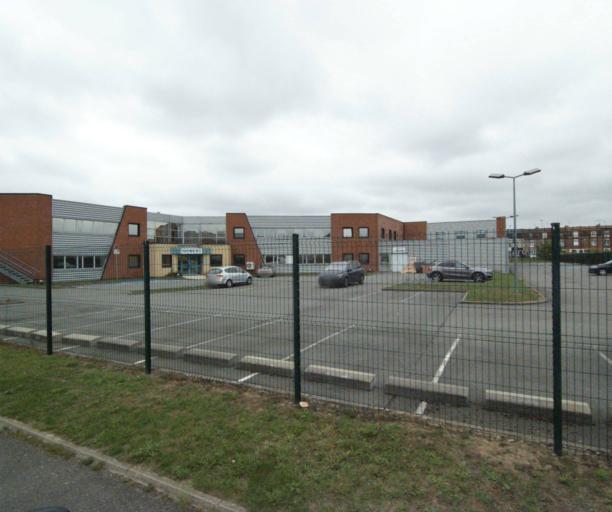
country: FR
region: Nord-Pas-de-Calais
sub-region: Departement du Nord
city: Lezennes
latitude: 50.6095
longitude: 3.1070
